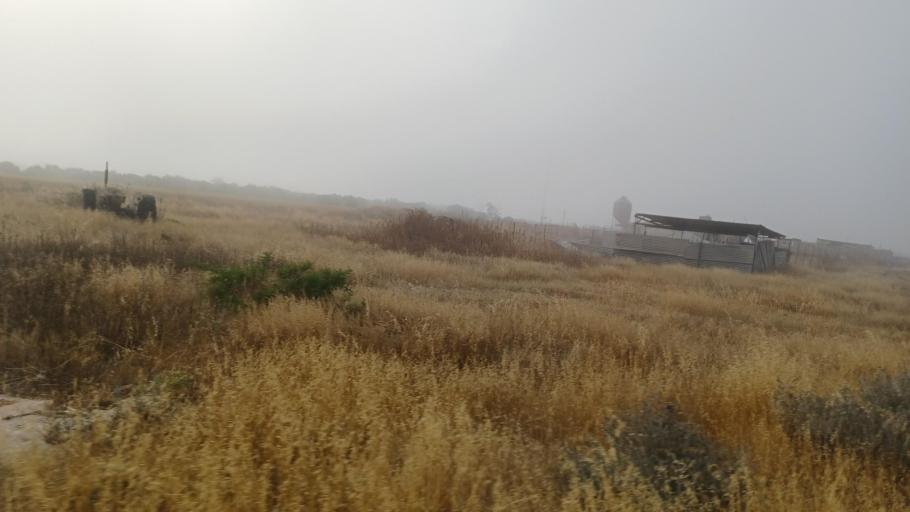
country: CY
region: Ammochostos
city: Acheritou
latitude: 35.1032
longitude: 33.8758
